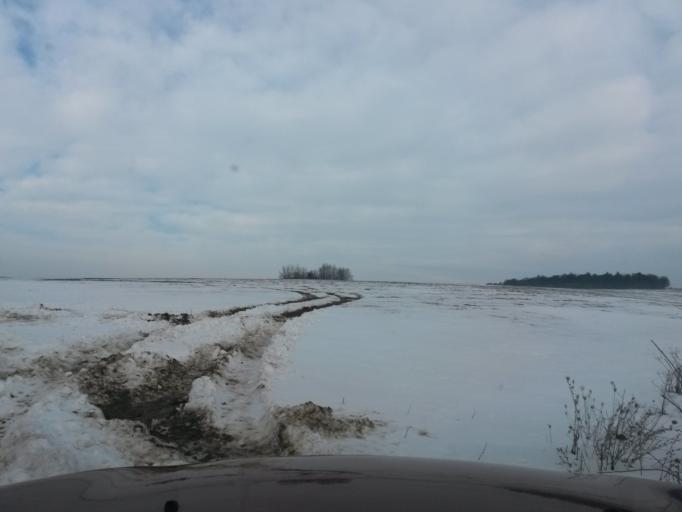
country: SK
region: Kosicky
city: Kosice
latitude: 48.7942
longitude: 21.3445
